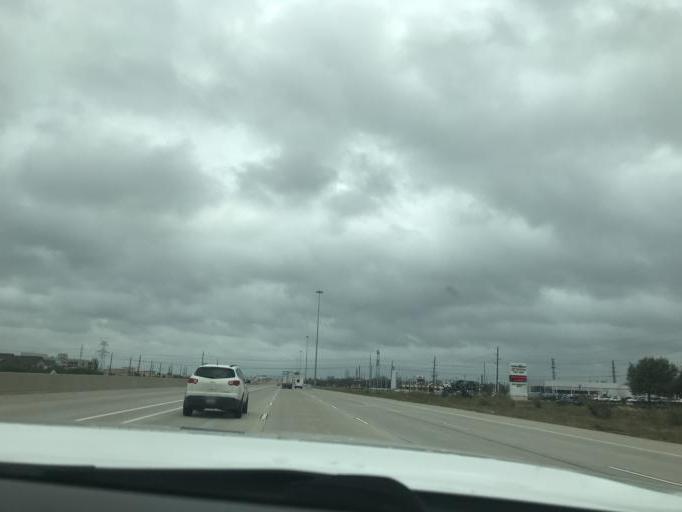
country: US
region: Texas
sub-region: Fort Bend County
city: Greatwood
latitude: 29.5594
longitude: -95.6981
